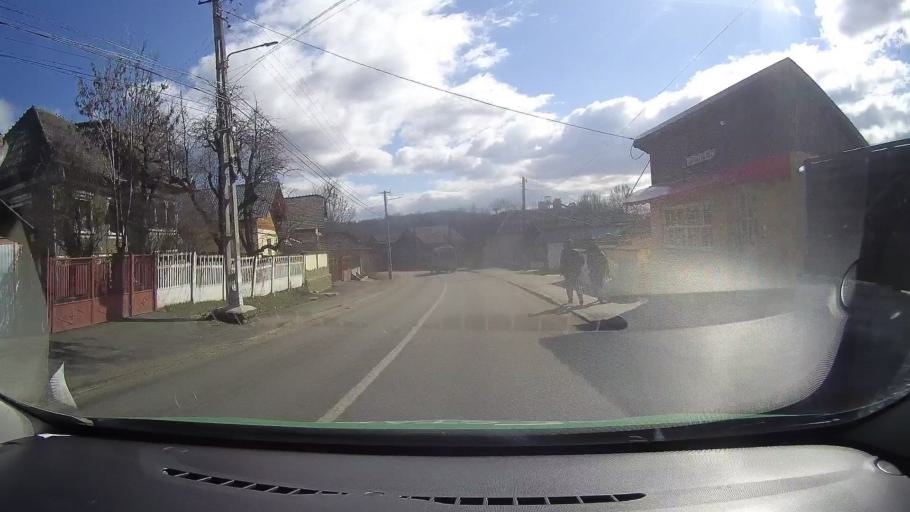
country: RO
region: Dambovita
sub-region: Comuna Fieni
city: Fieni
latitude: 45.1292
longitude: 25.4111
